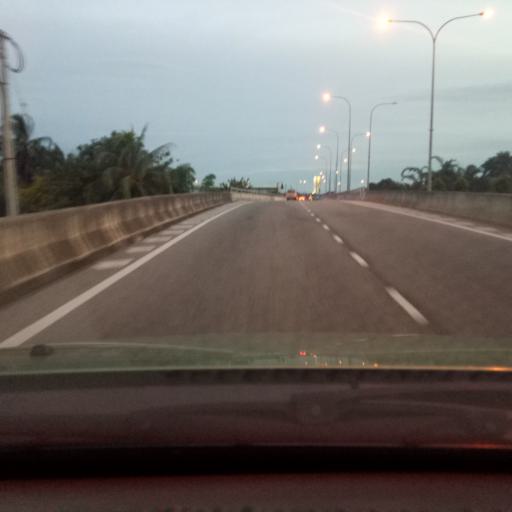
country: MY
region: Kedah
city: Alor Setar
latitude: 6.0999
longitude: 100.3737
